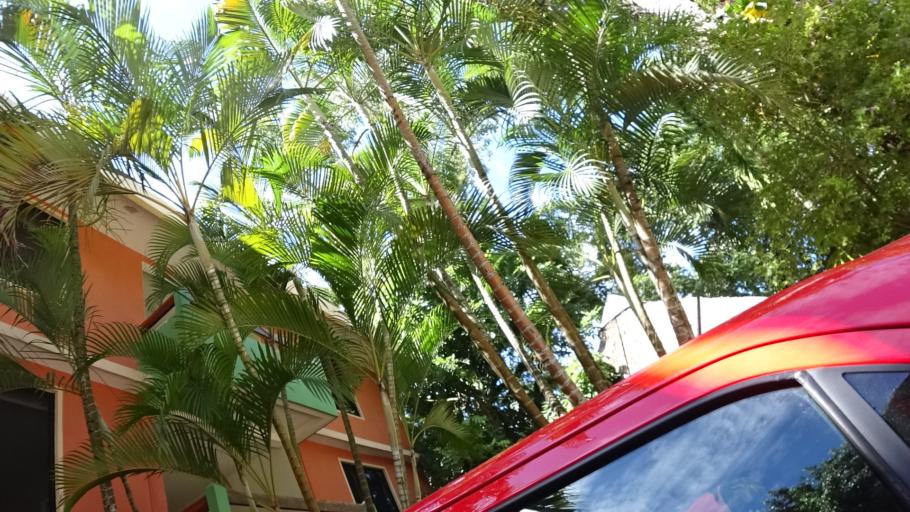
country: MX
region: Chiapas
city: Palenque
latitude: 17.5097
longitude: -91.9893
